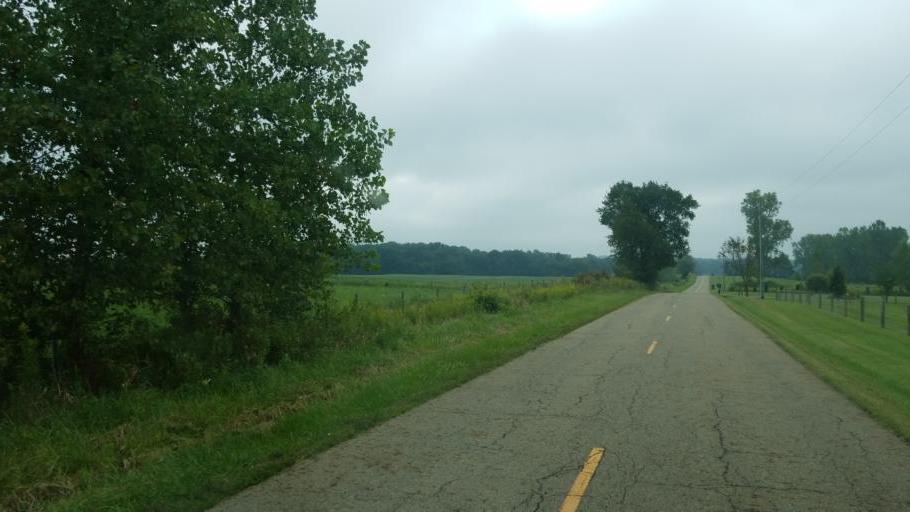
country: US
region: Ohio
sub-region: Licking County
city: Utica
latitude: 40.3081
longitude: -82.4511
